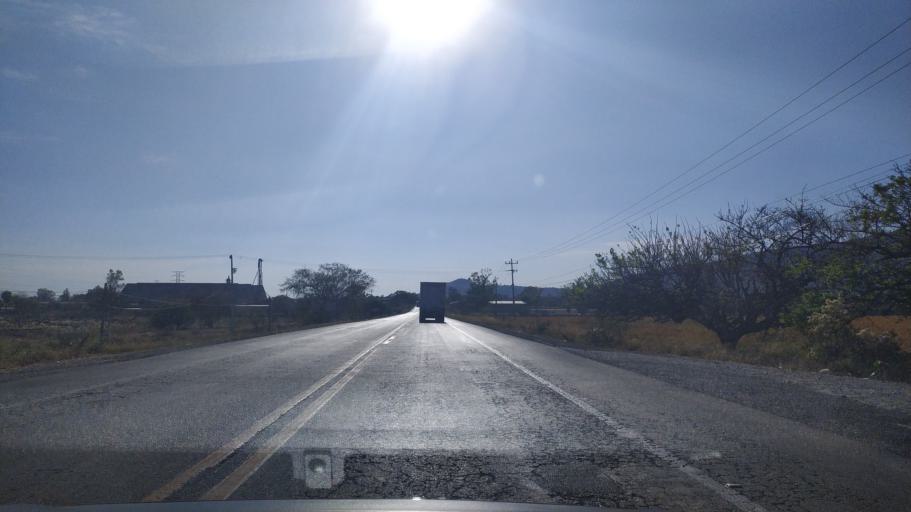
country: MX
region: Jalisco
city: Jamay
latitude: 20.2939
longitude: -102.6621
